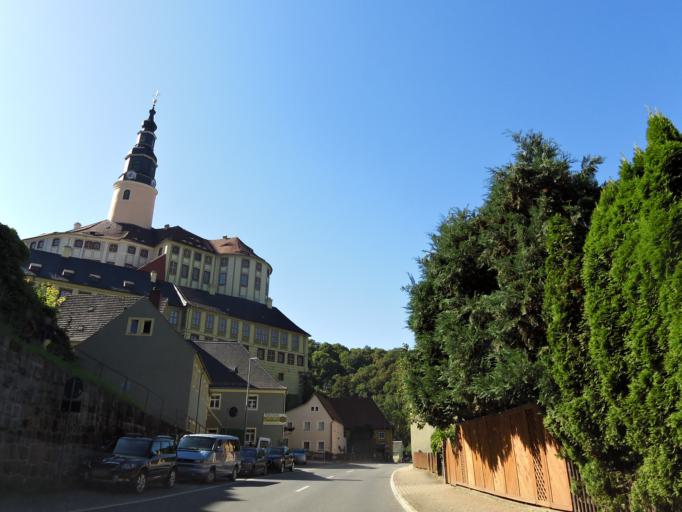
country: DE
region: Saxony
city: Dohna
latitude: 50.9327
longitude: 13.8604
